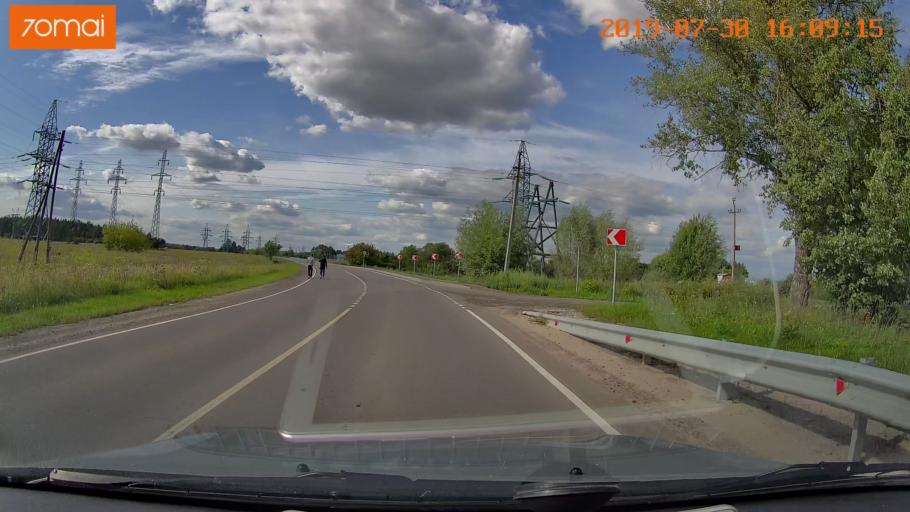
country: RU
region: Moskovskaya
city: Peski
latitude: 55.2519
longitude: 38.7197
